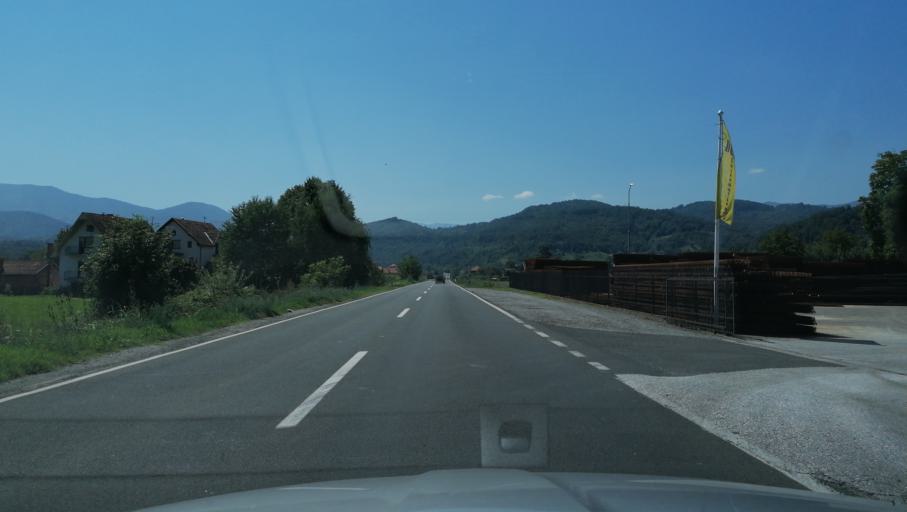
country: RS
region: Central Serbia
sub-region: Raski Okrug
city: Kraljevo
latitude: 43.6916
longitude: 20.5805
